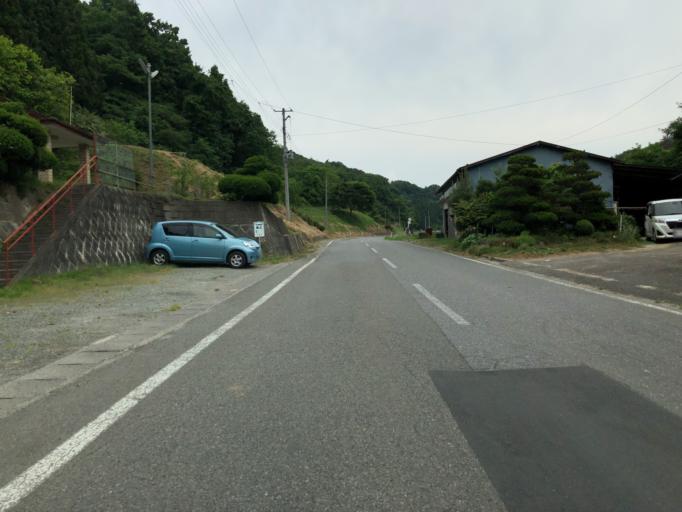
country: JP
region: Fukushima
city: Miharu
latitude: 37.4600
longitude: 140.5226
